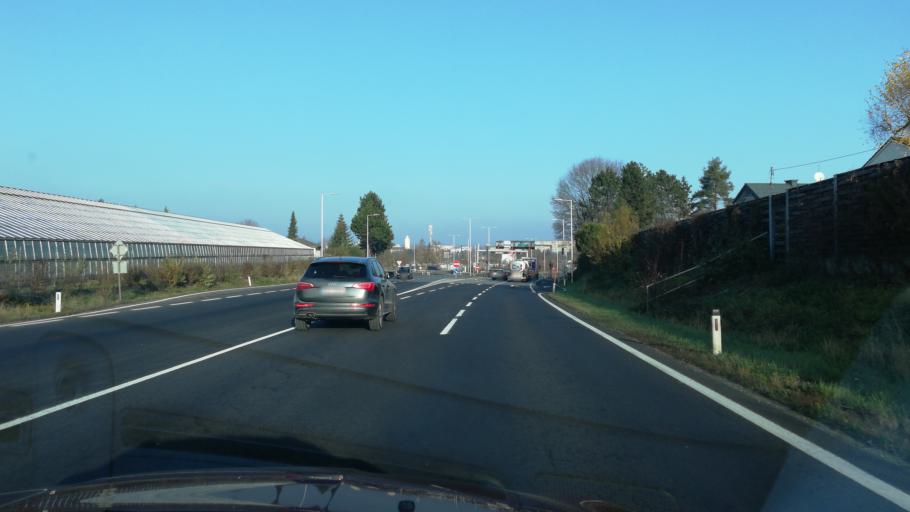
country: AT
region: Upper Austria
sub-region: Wels-Land
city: Thalheim bei Wels
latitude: 48.1498
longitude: 14.0448
